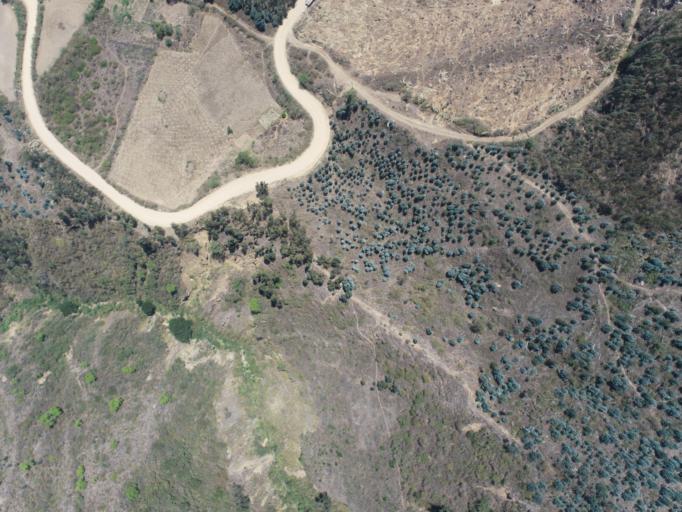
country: BO
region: La Paz
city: Quime
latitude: -16.9028
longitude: -67.1398
